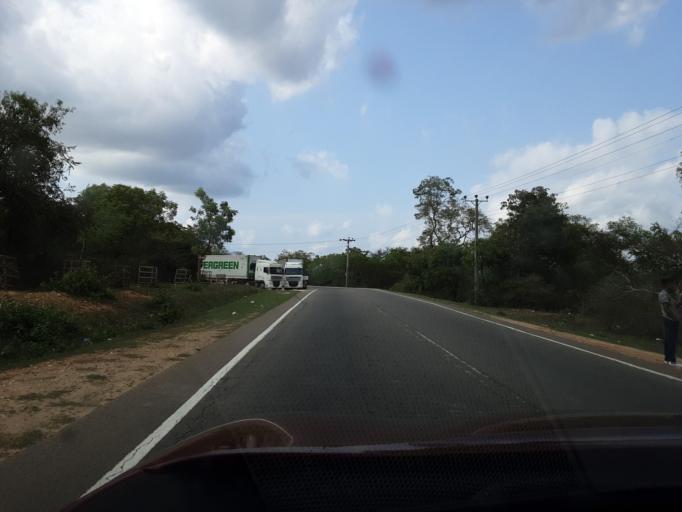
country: LK
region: Uva
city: Haputale
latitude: 6.5074
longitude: 81.1304
